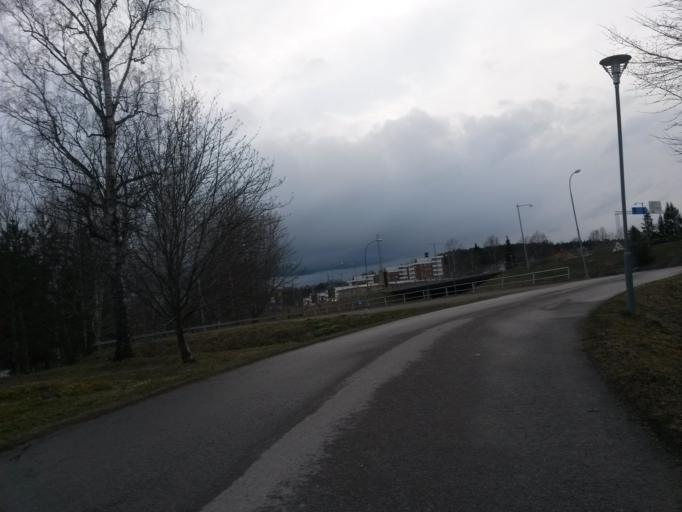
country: SE
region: OErebro
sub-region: Karlskoga Kommun
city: Karlskoga
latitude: 59.3247
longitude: 14.5360
